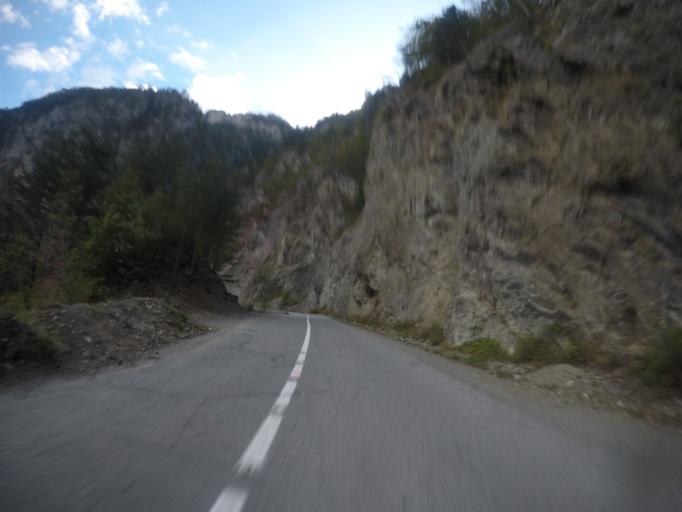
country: ME
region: Mojkovac
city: Mojkovac
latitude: 43.0147
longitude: 19.4085
